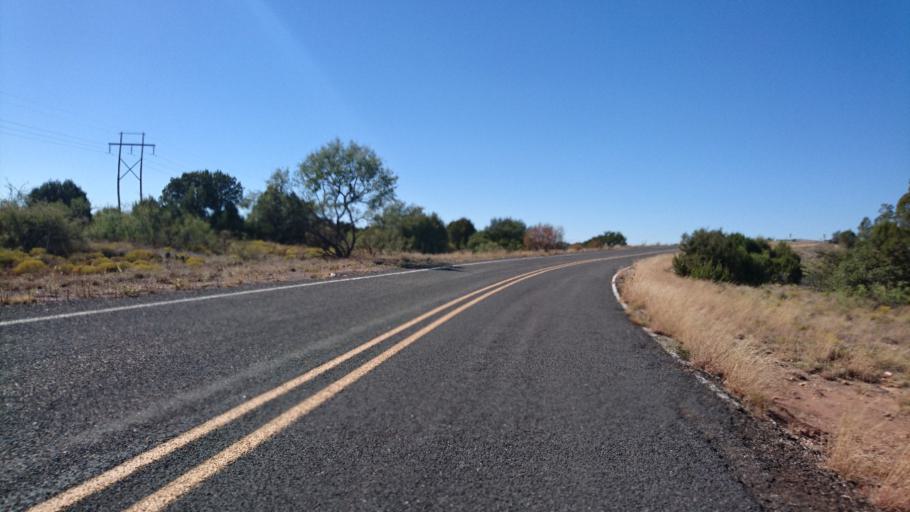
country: US
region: New Mexico
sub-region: Quay County
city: Tucumcari
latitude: 35.0658
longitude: -104.1772
